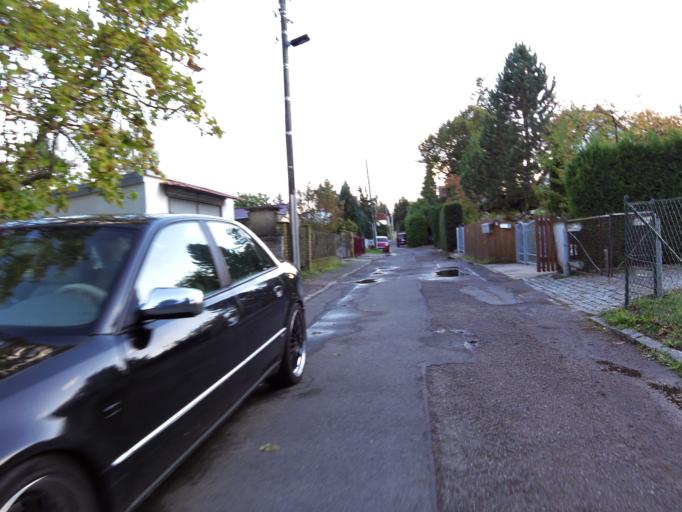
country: DE
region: Saxony
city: Taucha
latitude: 51.3261
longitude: 12.4621
